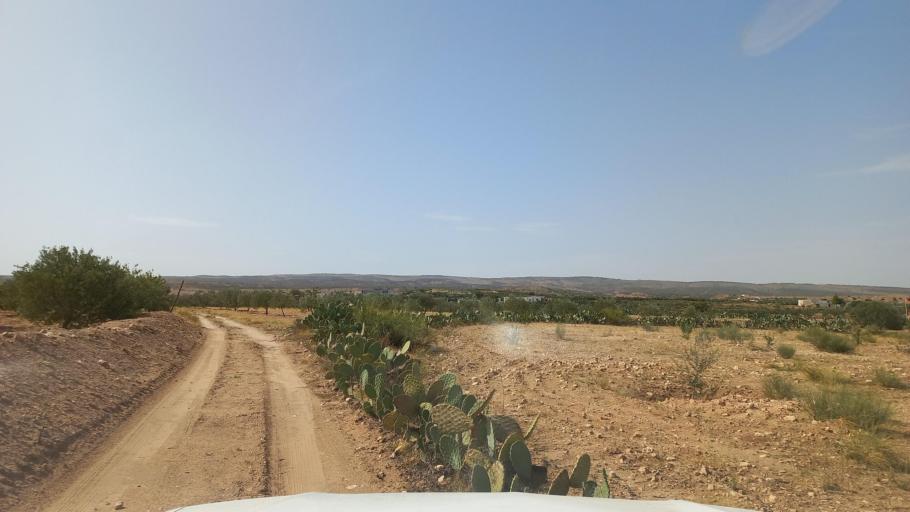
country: TN
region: Al Qasrayn
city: Kasserine
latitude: 35.2963
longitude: 8.9476
